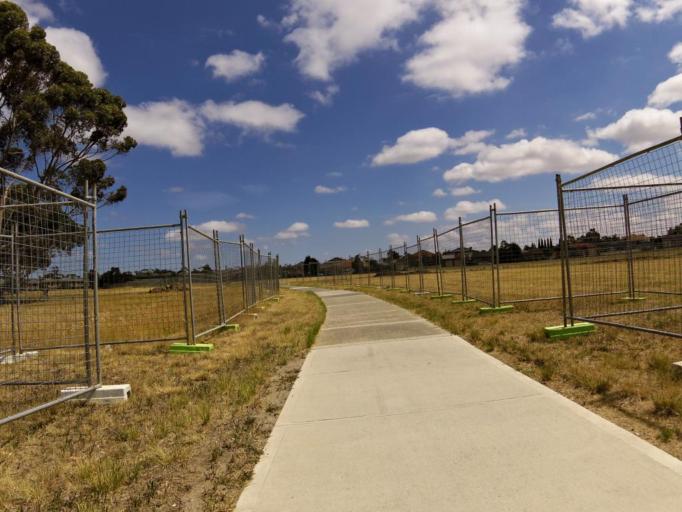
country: AU
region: Victoria
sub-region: Hume
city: Roxburgh Park
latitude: -37.6199
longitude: 144.9281
